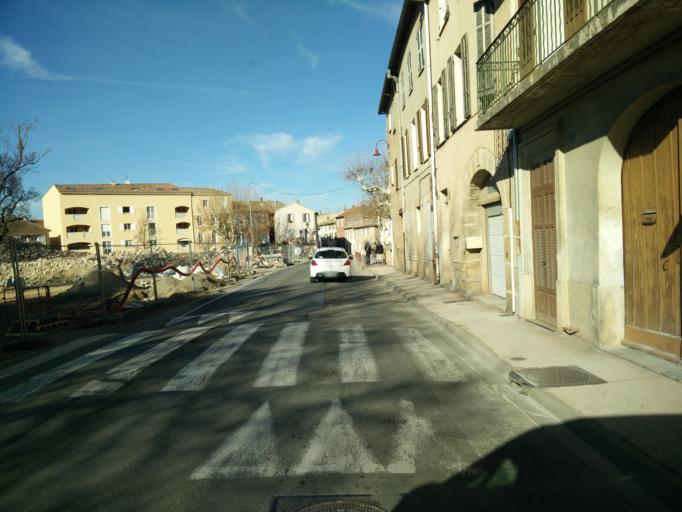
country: FR
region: Provence-Alpes-Cote d'Azur
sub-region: Departement du Var
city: Vidauban
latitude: 43.4246
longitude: 6.4311
